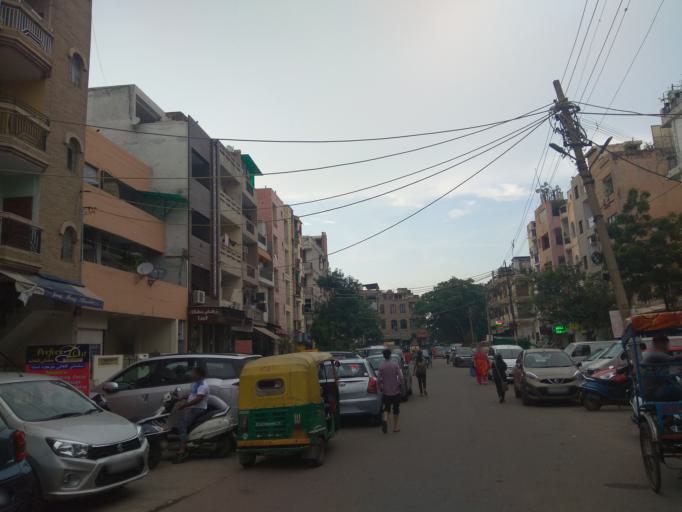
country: IN
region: NCT
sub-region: New Delhi
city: New Delhi
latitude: 28.5719
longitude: 77.2432
